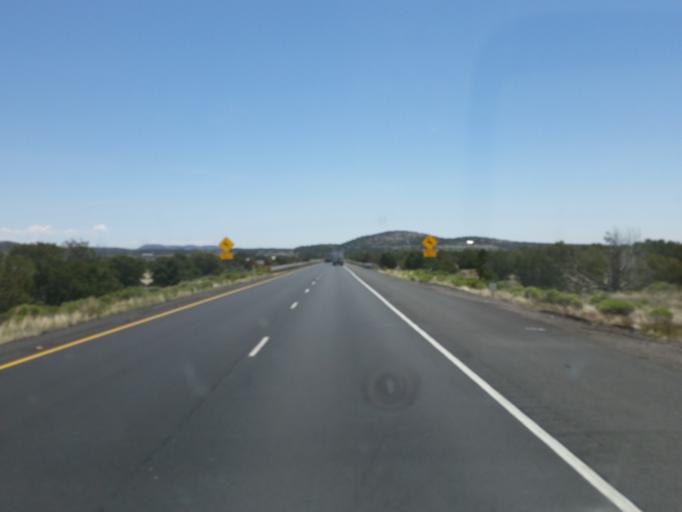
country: US
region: Arizona
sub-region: Coconino County
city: Flagstaff
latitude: 35.2016
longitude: -111.4425
